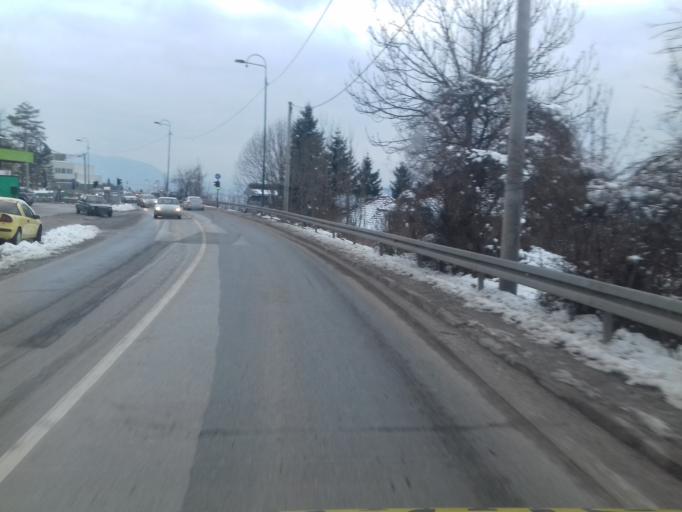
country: BA
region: Federation of Bosnia and Herzegovina
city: Kobilja Glava
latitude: 43.8545
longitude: 18.4254
